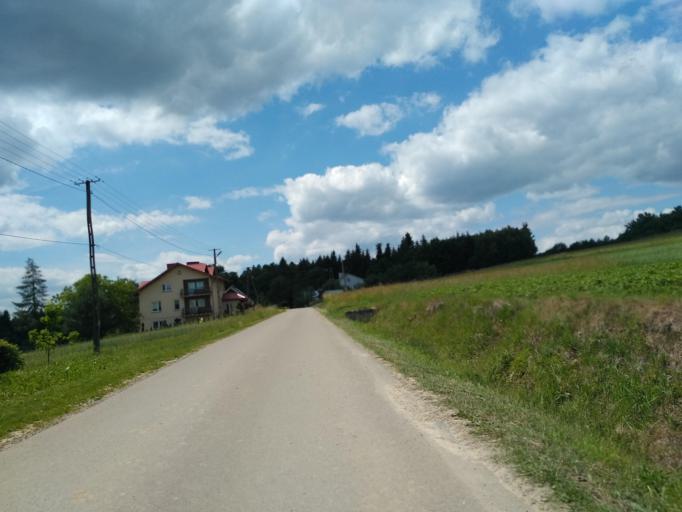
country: PL
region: Subcarpathian Voivodeship
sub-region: Powiat brzozowski
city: Wesola
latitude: 49.7588
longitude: 22.1327
